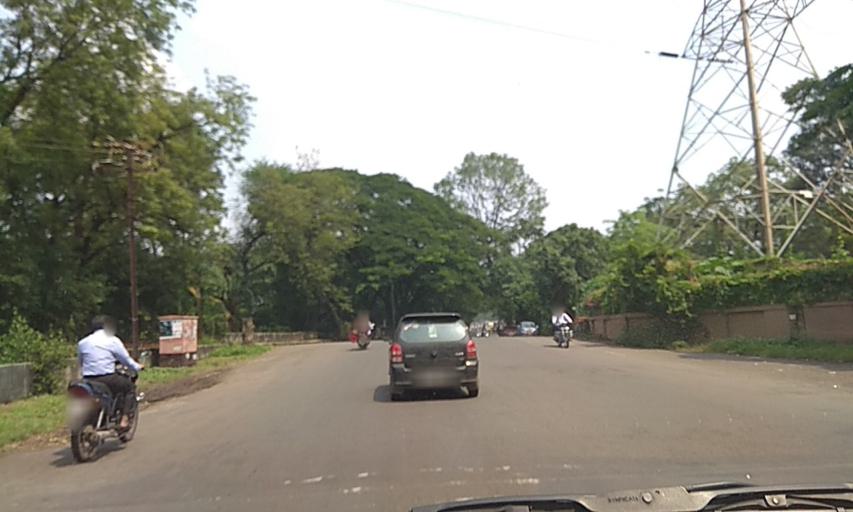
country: IN
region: Maharashtra
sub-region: Pune Division
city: Shivaji Nagar
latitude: 18.5382
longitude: 73.8060
